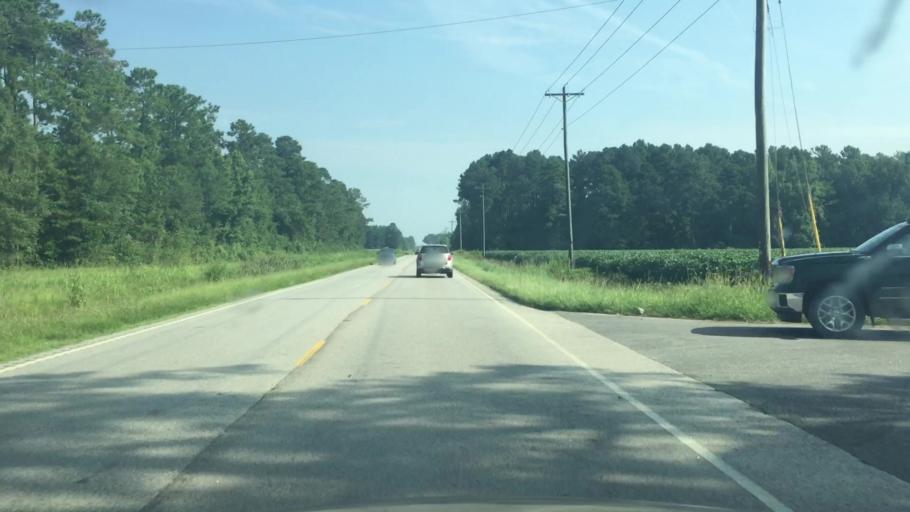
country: US
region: North Carolina
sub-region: Columbus County
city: Tabor City
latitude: 34.1217
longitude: -78.8758
